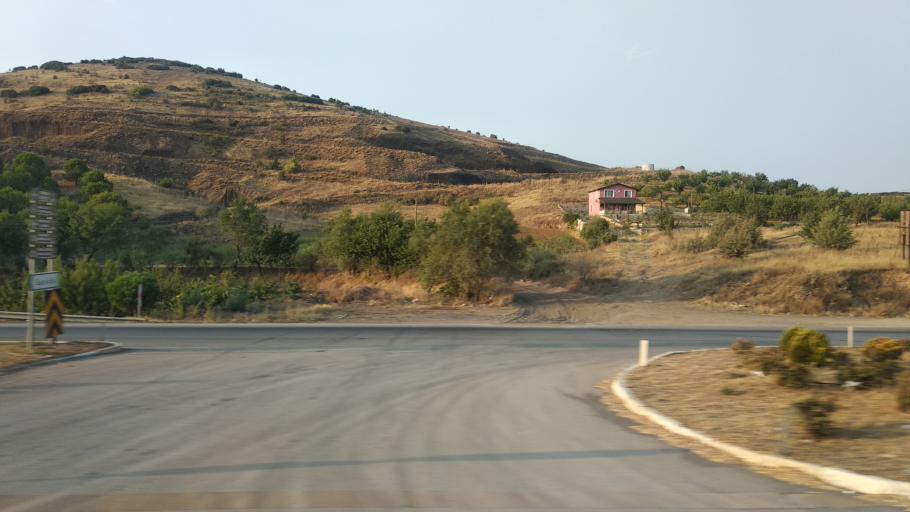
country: TR
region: Manisa
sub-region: Kula
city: Kula
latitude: 38.5679
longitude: 28.5774
